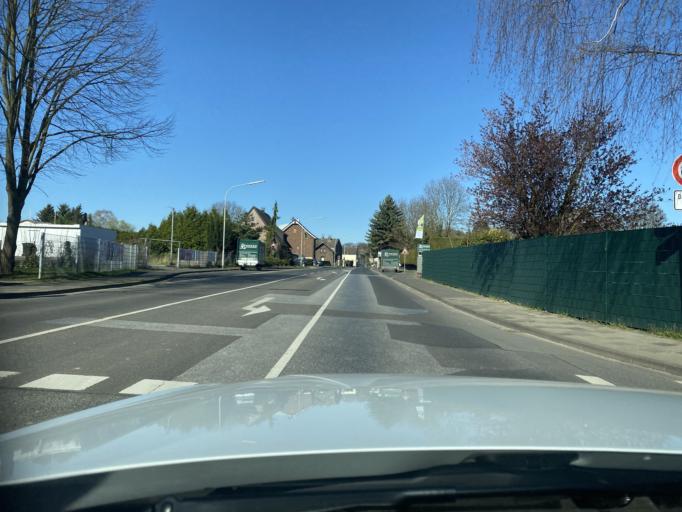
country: DE
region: North Rhine-Westphalia
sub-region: Regierungsbezirk Dusseldorf
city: Grevenbroich
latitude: 51.1039
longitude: 6.5908
